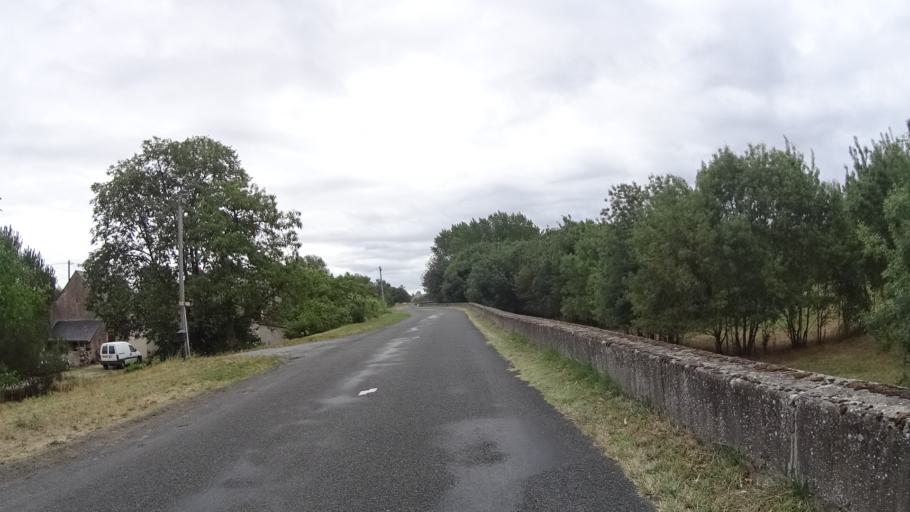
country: FR
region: Pays de la Loire
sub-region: Departement de Maine-et-Loire
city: Chalonnes-sur-Loire
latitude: 47.3661
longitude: -0.7331
